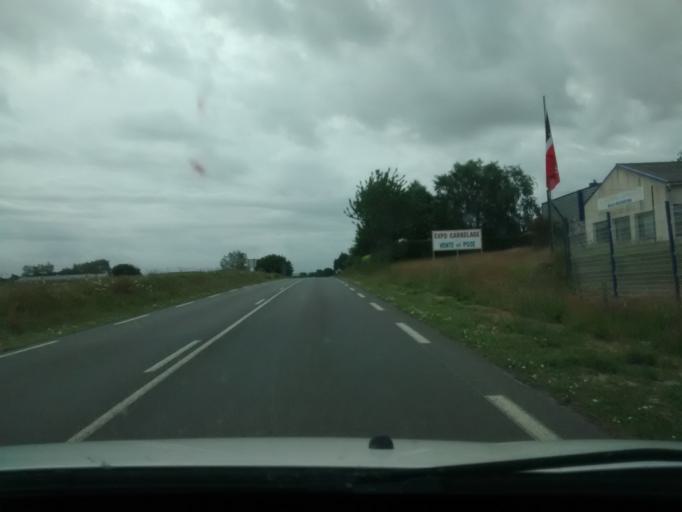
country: FR
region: Brittany
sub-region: Departement des Cotes-d'Armor
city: Trelevern
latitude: 48.7754
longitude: -3.3729
